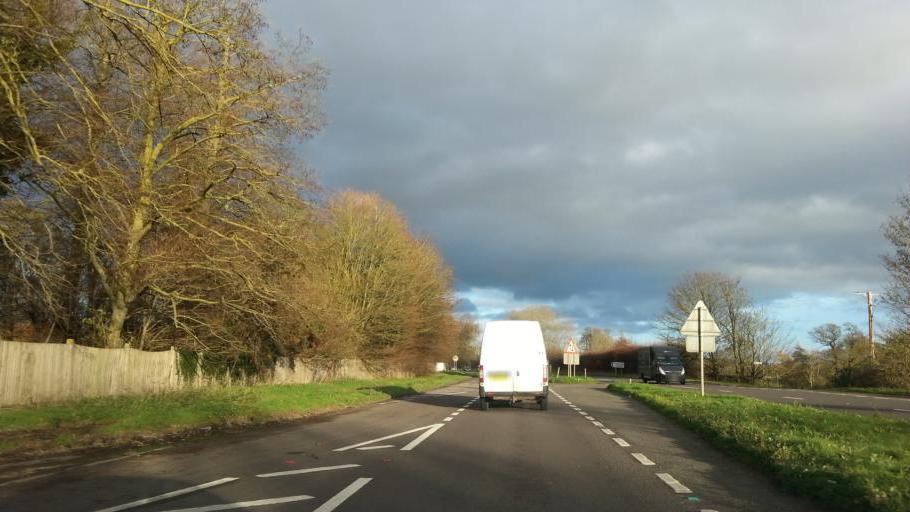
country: GB
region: England
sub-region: Oxfordshire
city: Marcham
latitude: 51.7051
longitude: -1.3433
